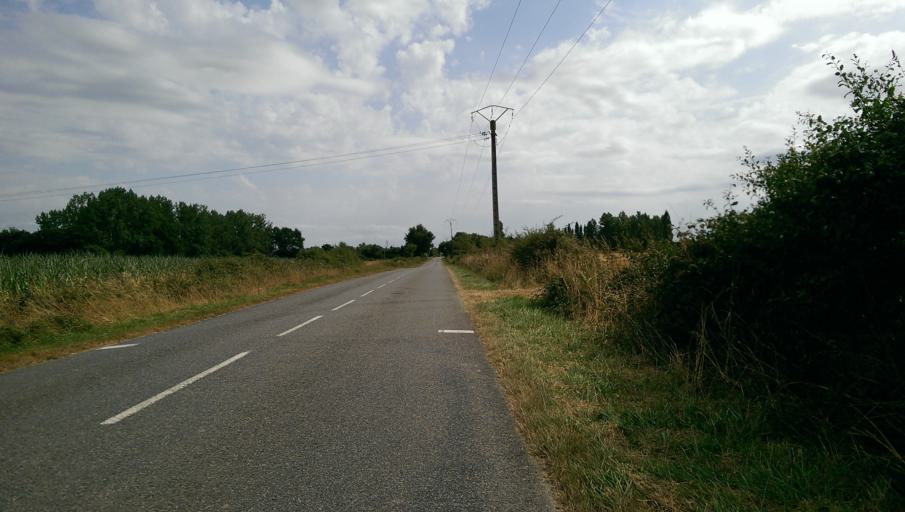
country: FR
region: Pays de la Loire
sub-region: Departement de la Loire-Atlantique
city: La Planche
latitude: 46.9944
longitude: -1.4285
